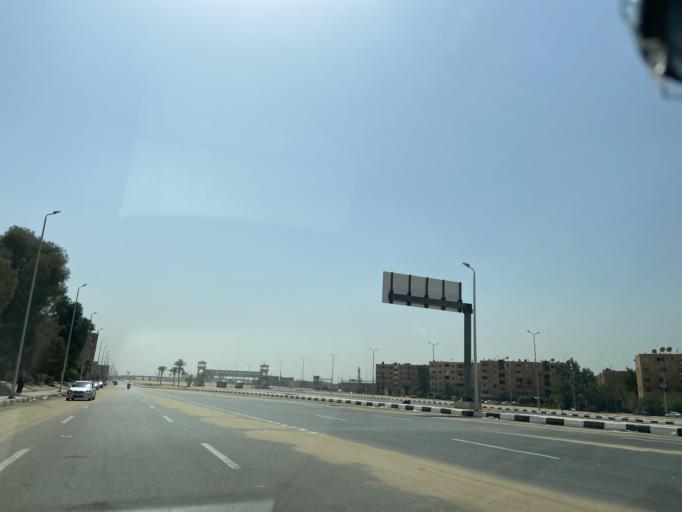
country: EG
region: Muhafazat al Qahirah
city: Cairo
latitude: 30.0450
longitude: 31.3643
